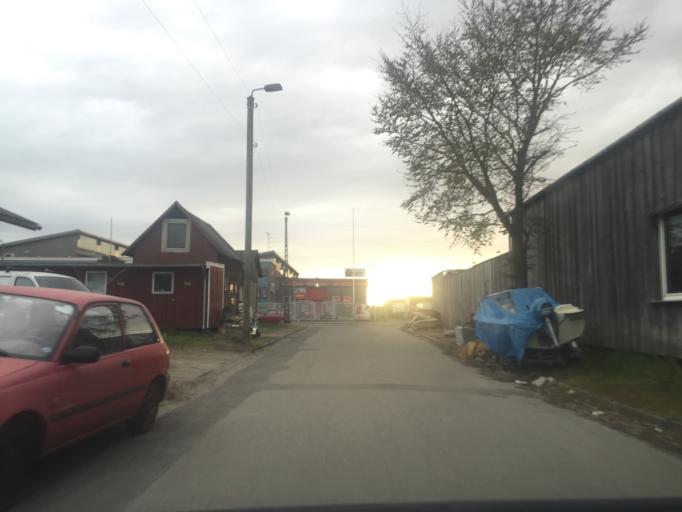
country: DK
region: Capital Region
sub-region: Frederiksberg Kommune
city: Frederiksberg
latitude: 55.6408
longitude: 12.5408
